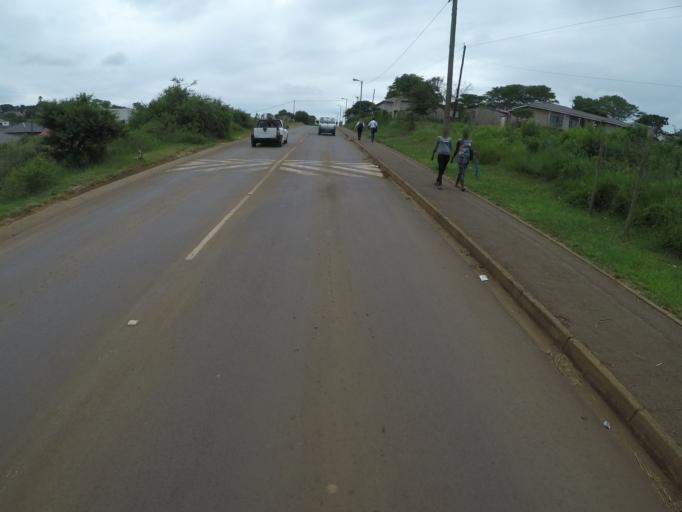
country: ZA
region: KwaZulu-Natal
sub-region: uThungulu District Municipality
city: Empangeni
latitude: -28.7811
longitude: 31.8630
